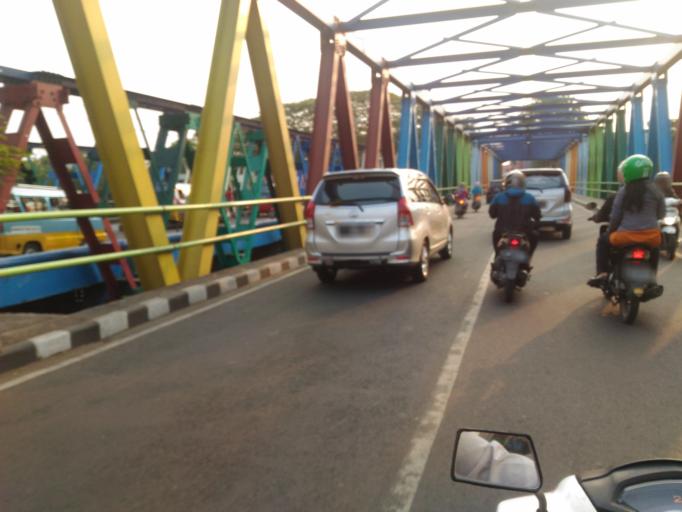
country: ID
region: Banten
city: Tangerang
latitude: -6.1755
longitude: 106.6292
